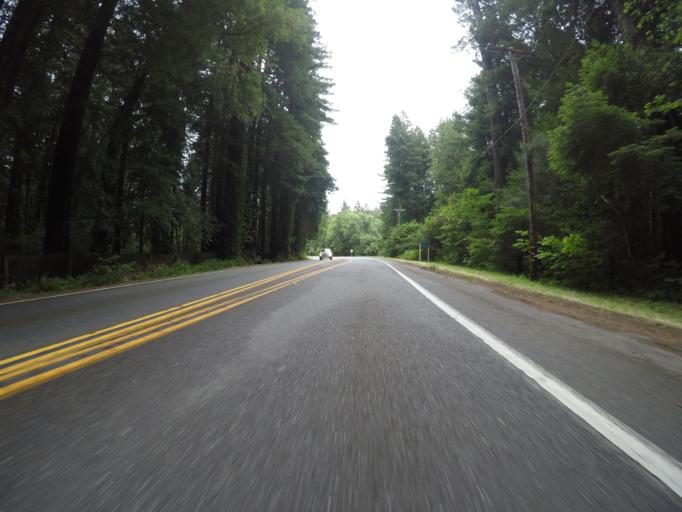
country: US
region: California
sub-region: Humboldt County
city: Rio Dell
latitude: 40.3992
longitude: -123.9481
